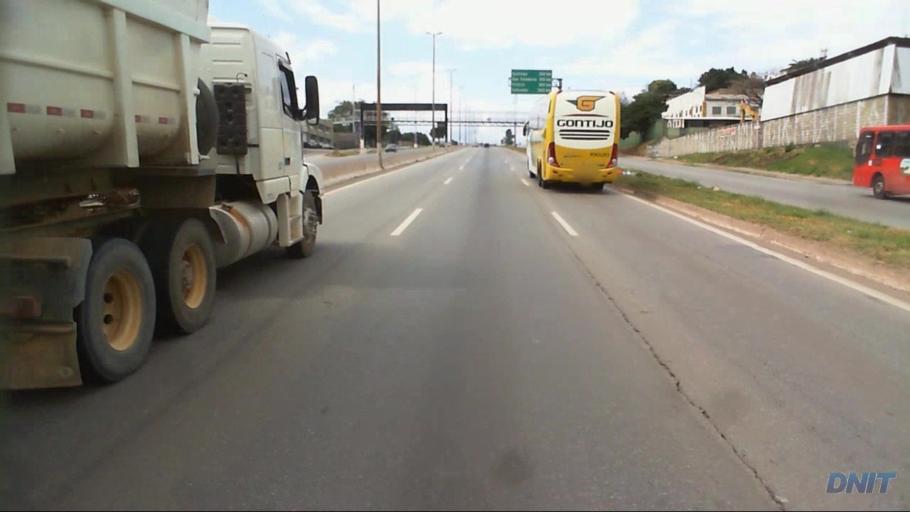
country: BR
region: Minas Gerais
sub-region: Belo Horizonte
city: Belo Horizonte
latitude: -19.8612
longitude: -43.9203
